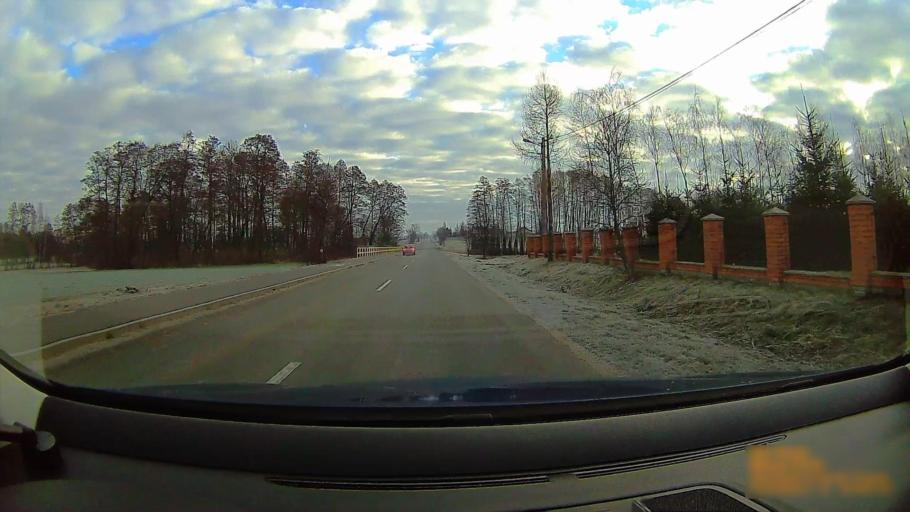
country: PL
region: Greater Poland Voivodeship
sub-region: Powiat koninski
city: Rzgow Pierwszy
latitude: 52.1631
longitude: 18.0679
